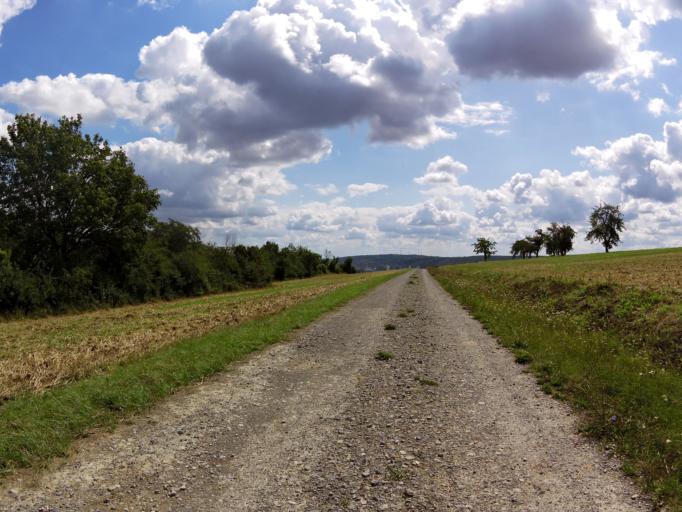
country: DE
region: Bavaria
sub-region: Regierungsbezirk Unterfranken
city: Margetshochheim
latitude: 49.8359
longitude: 9.8506
